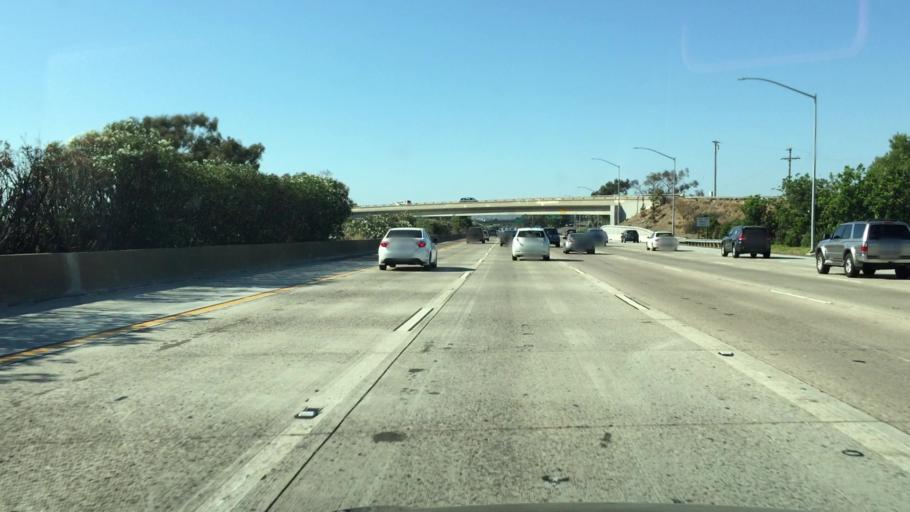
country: US
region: California
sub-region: San Diego County
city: San Diego
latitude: 32.7638
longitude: -117.2051
